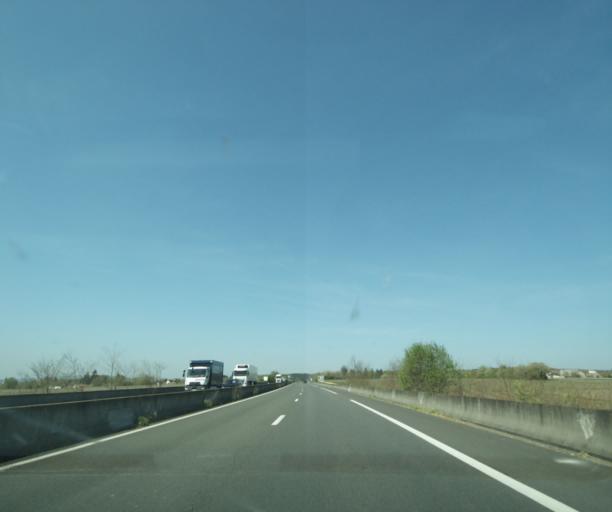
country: FR
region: Bourgogne
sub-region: Departement de la Nievre
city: Pouilly-sur-Loire
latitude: 47.2824
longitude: 2.9703
